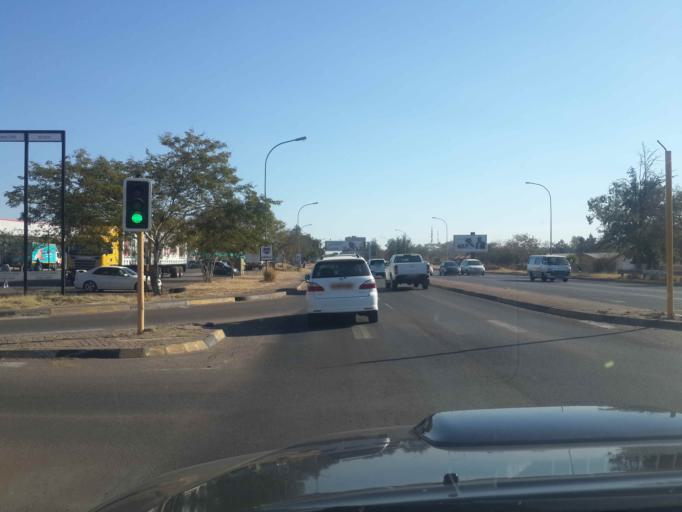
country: BW
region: South East
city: Gaborone
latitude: -24.6744
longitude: 25.9068
